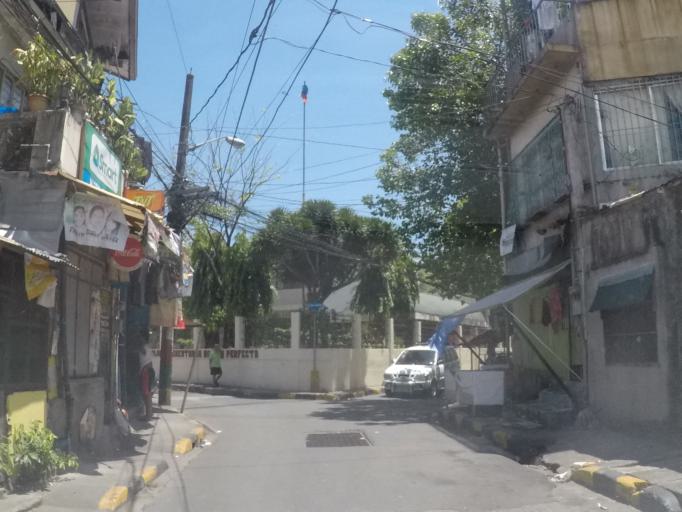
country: PH
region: Metro Manila
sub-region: San Juan
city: San Juan
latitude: 14.6037
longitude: 121.0231
